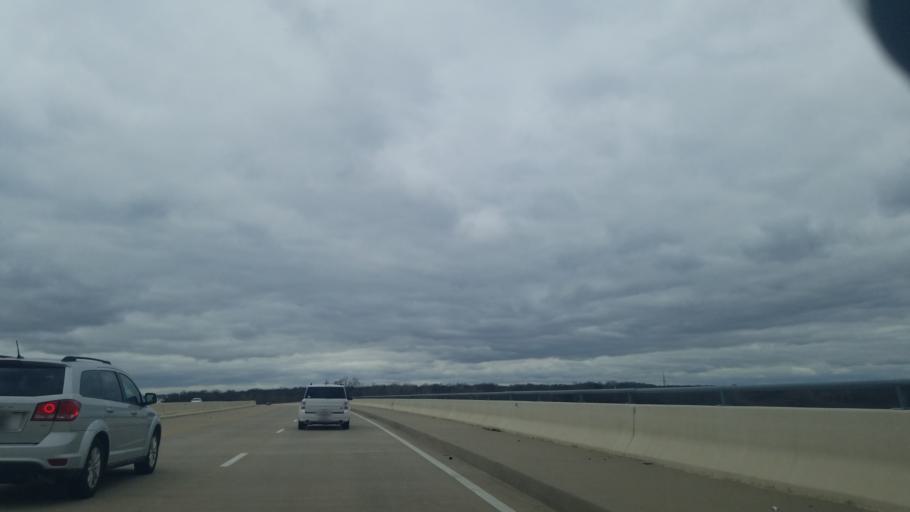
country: US
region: Texas
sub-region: Denton County
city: Copper Canyon
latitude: 33.1205
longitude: -97.0808
